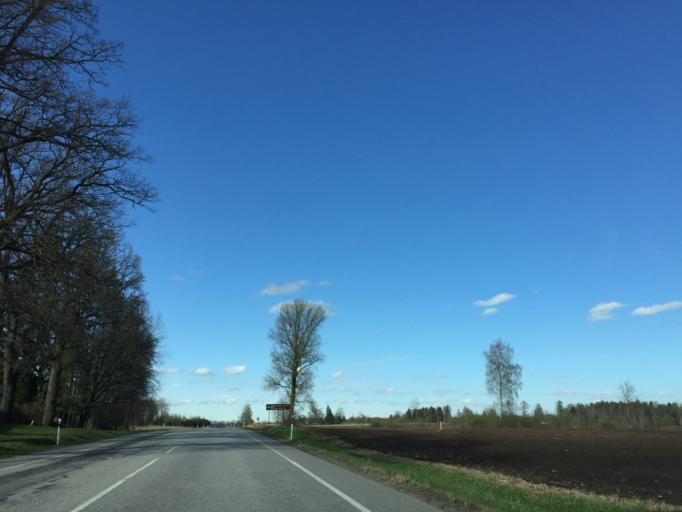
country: EE
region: Vorumaa
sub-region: Antsla vald
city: Vana-Antsla
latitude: 57.8911
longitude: 26.2884
